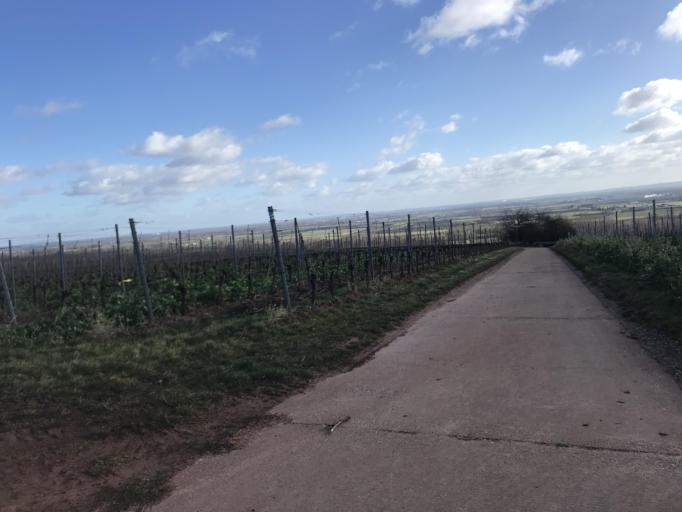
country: DE
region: Rheinland-Pfalz
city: Nackenheim
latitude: 49.8991
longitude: 8.3366
